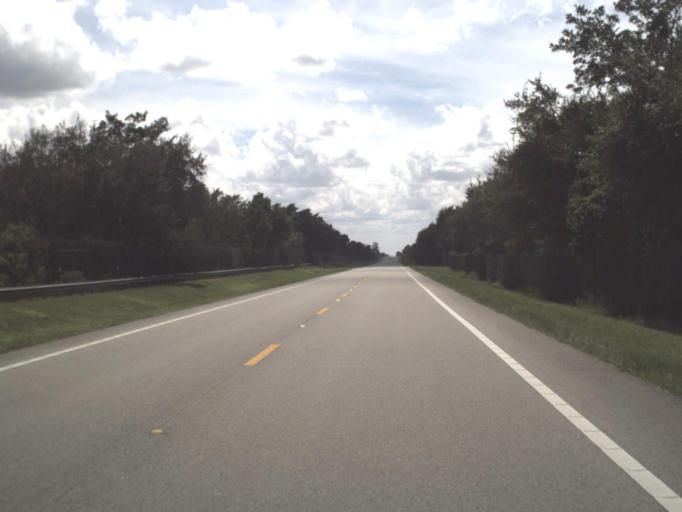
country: US
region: Florida
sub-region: Collier County
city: Immokalee
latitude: 26.2024
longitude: -81.3462
